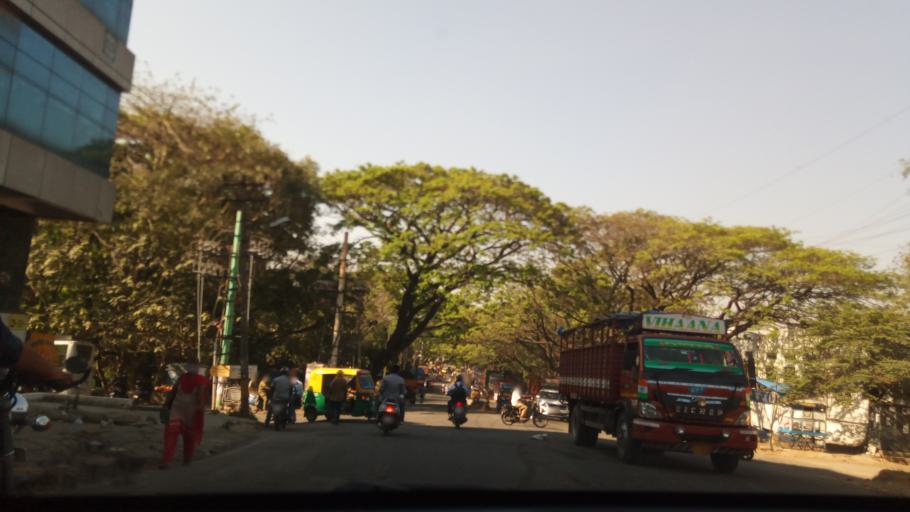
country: IN
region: Karnataka
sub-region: Bangalore Urban
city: Bangalore
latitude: 13.0230
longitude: 77.5422
